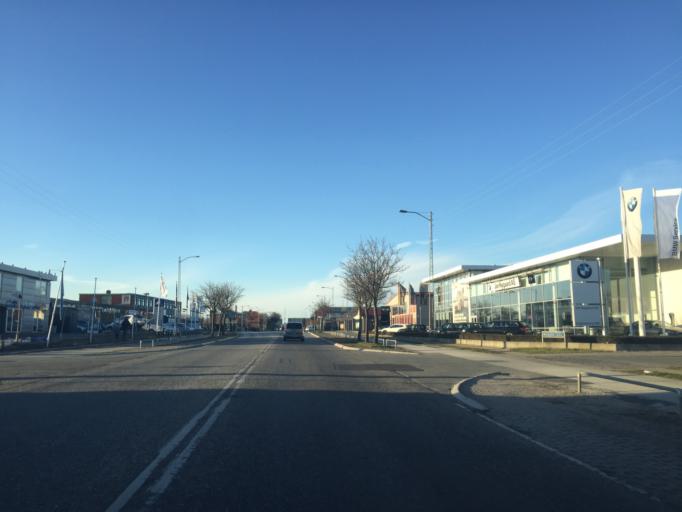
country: DK
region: Capital Region
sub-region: Tarnby Kommune
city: Tarnby
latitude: 55.6213
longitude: 12.6048
